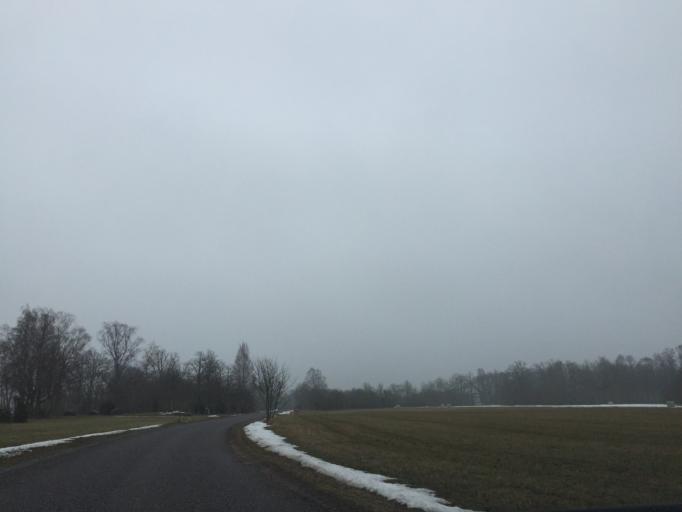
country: EE
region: Saare
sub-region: Kuressaare linn
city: Kuressaare
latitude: 58.2742
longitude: 22.5738
